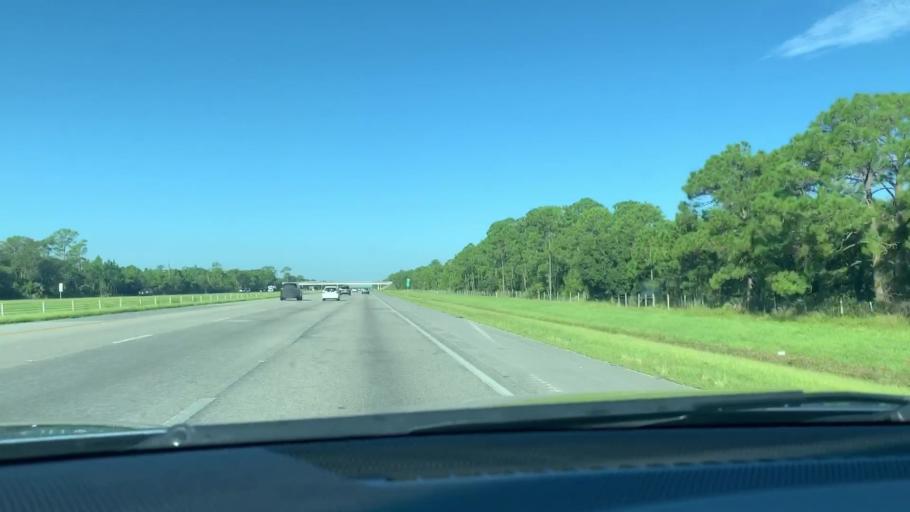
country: US
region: Florida
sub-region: Sarasota County
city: Warm Mineral Springs
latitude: 27.0999
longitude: -82.2254
